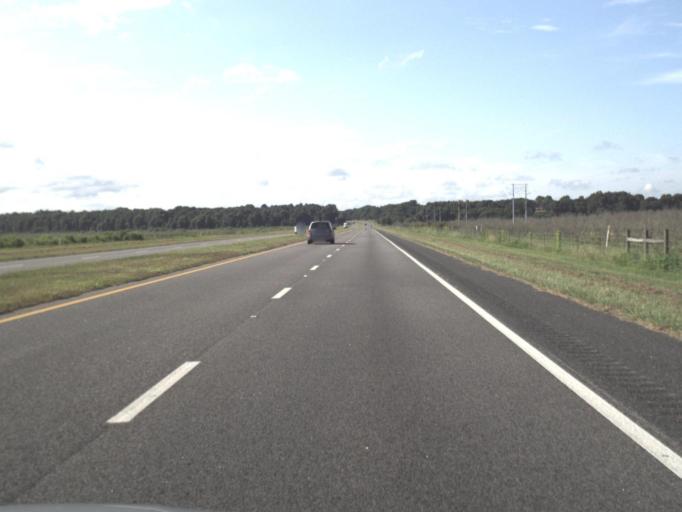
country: US
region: Florida
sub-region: Alachua County
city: Gainesville
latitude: 29.5709
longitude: -82.3345
